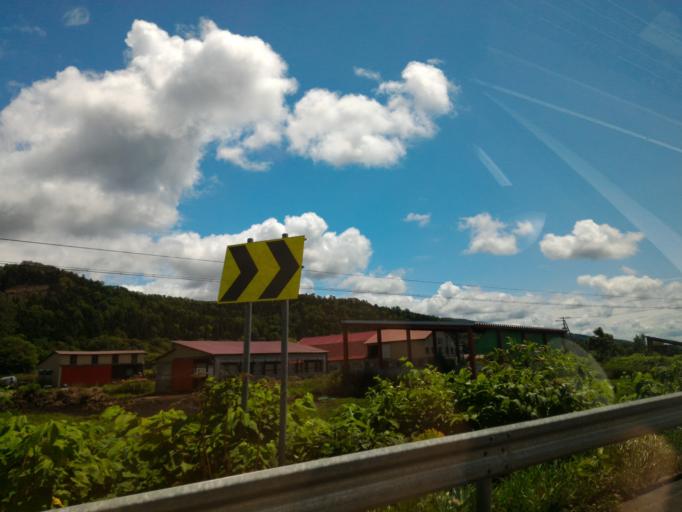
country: JP
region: Hokkaido
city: Nayoro
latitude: 44.5961
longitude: 142.3107
